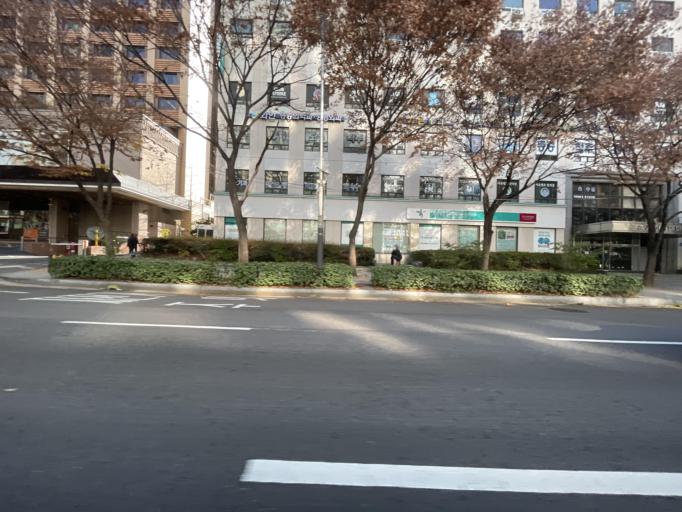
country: KR
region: Seoul
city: Seoul
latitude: 37.5406
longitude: 126.9476
